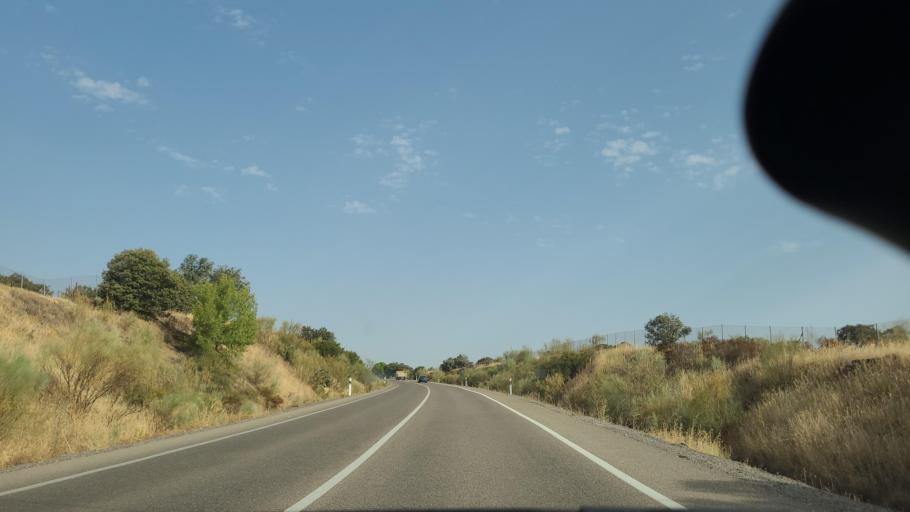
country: ES
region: Andalusia
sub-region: Province of Cordoba
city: Belmez
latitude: 38.2521
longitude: -5.1677
